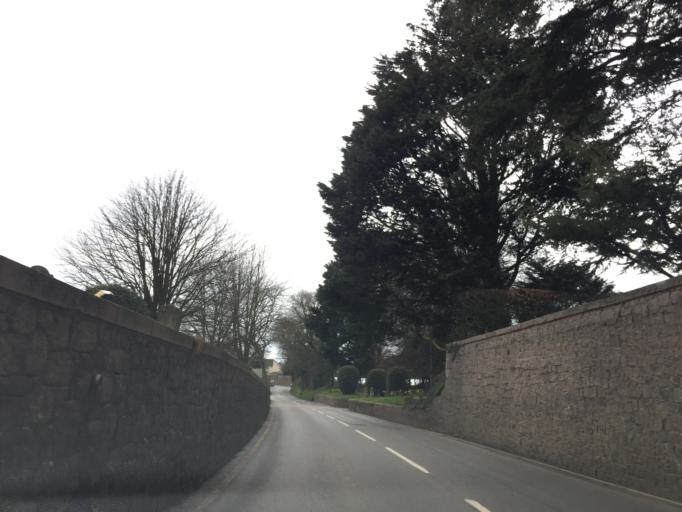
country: JE
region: St Helier
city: Saint Helier
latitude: 49.2352
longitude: -2.1735
